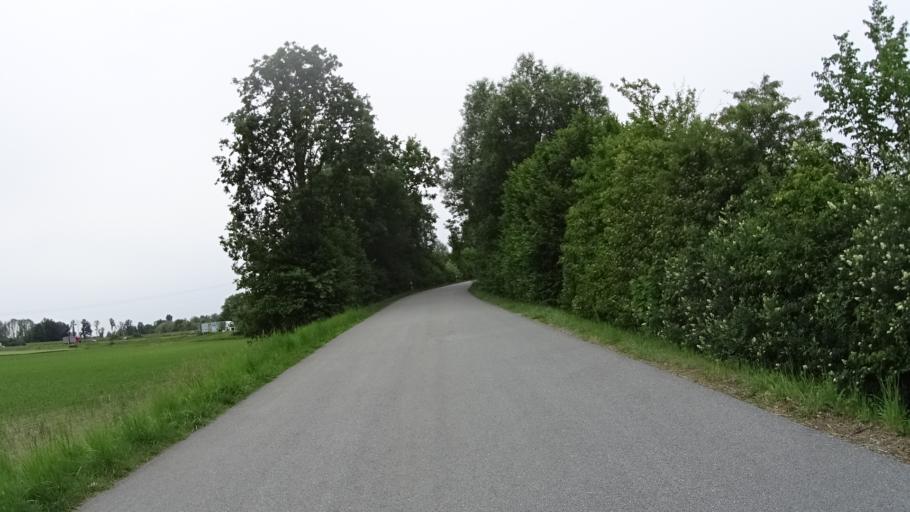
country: DE
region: Bavaria
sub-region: Lower Bavaria
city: Niederalteich
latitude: 48.7928
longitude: 13.0036
